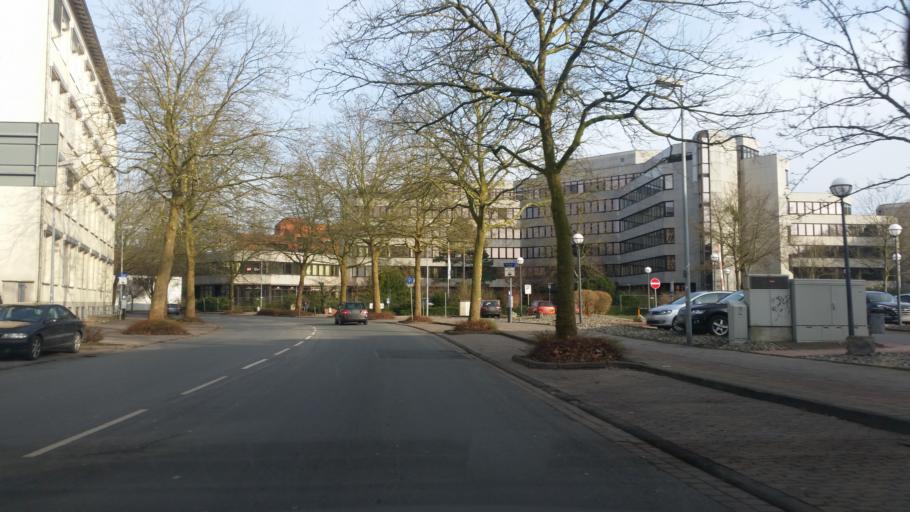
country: DE
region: Lower Saxony
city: Hameln
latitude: 52.1101
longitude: 9.3570
